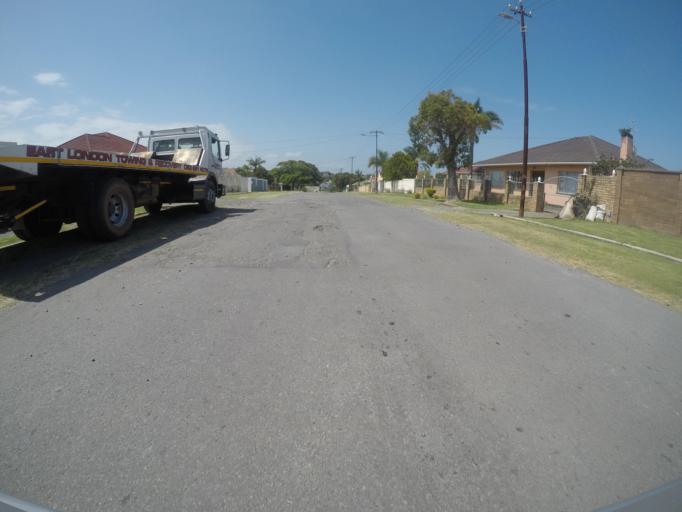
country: ZA
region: Eastern Cape
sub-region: Buffalo City Metropolitan Municipality
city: East London
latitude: -32.9776
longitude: 27.8722
